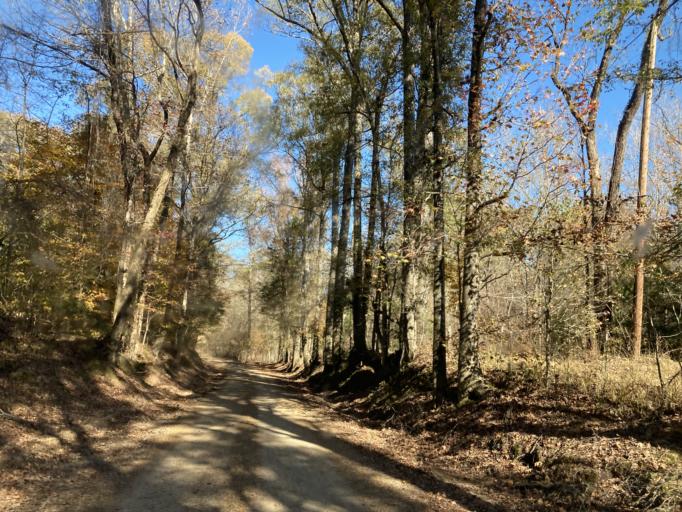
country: US
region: Mississippi
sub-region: Hinds County
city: Lynchburg
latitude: 32.5549
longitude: -90.4998
